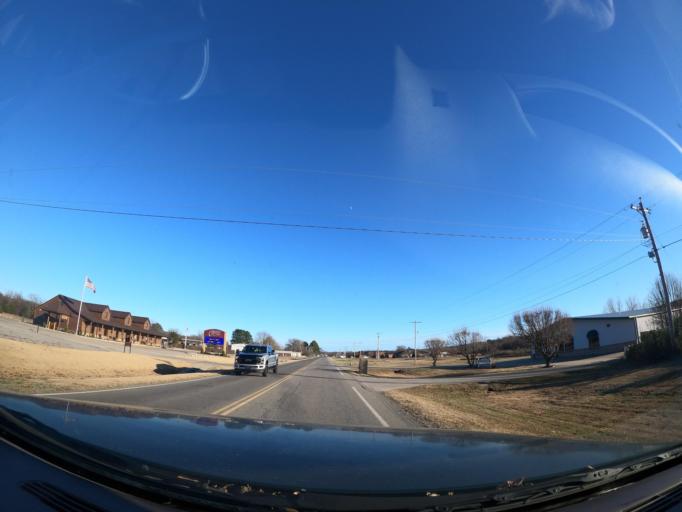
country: US
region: Oklahoma
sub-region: Latimer County
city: Wilburton
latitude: 34.9230
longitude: -95.3269
